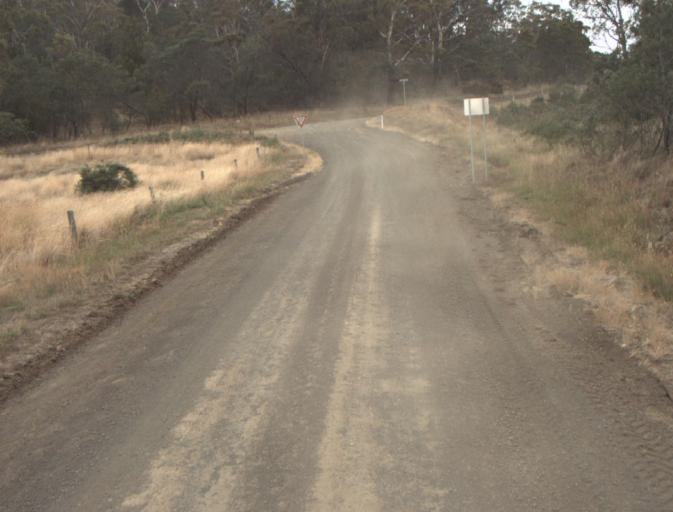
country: AU
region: Tasmania
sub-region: Northern Midlands
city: Evandale
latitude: -41.5231
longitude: 147.3667
